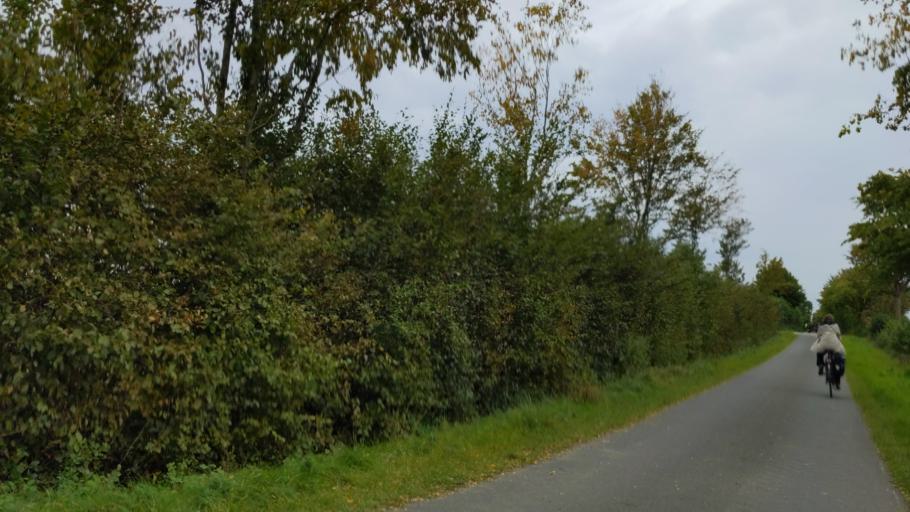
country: DE
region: Schleswig-Holstein
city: Bak
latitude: 53.7267
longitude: 10.7812
